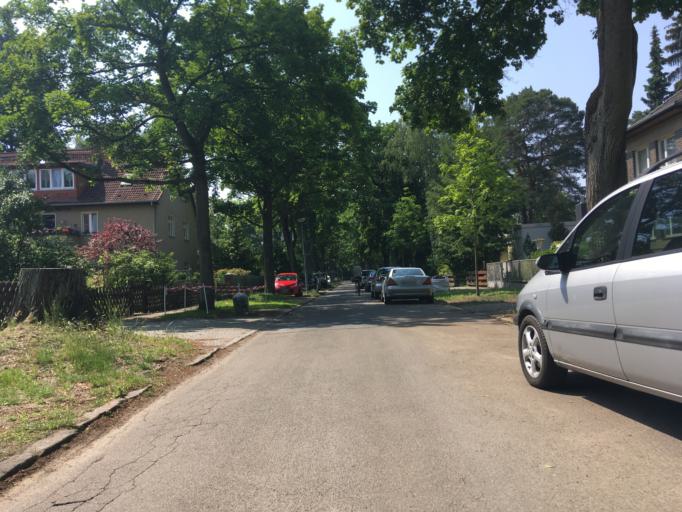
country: DE
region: Berlin
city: Konradshohe
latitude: 52.5847
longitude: 13.2318
